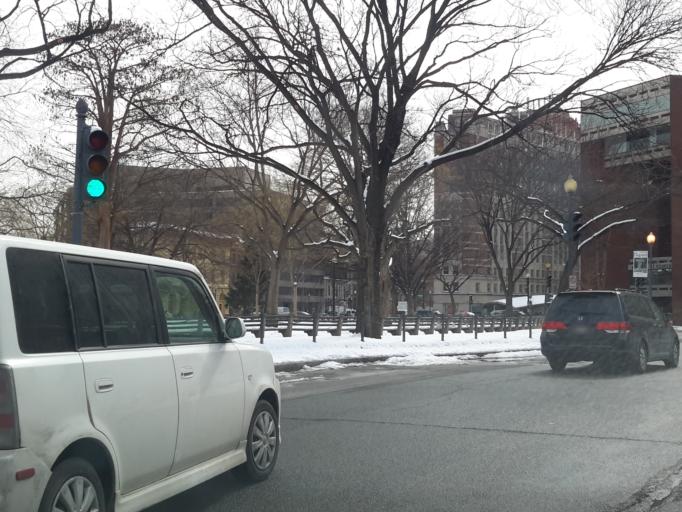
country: US
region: Washington, D.C.
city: Washington, D.C.
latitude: 38.9098
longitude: -77.0442
